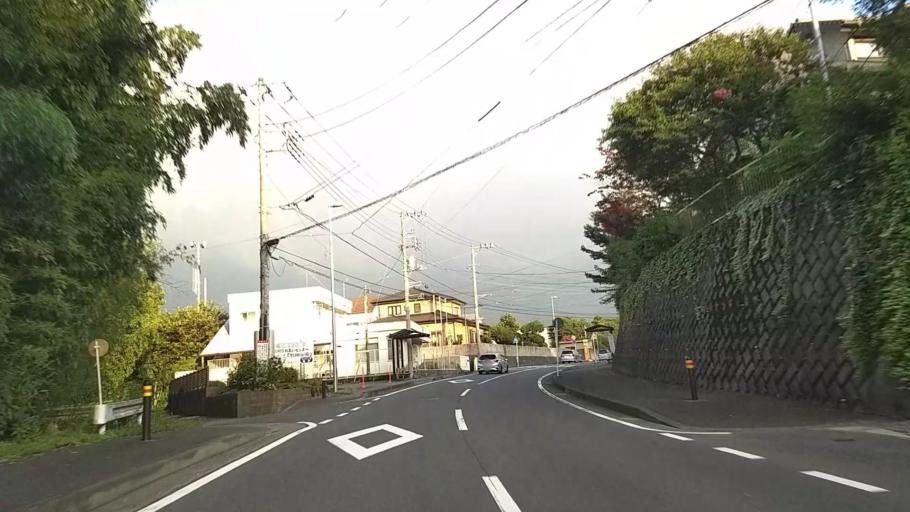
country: JP
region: Kanagawa
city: Atsugi
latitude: 35.4766
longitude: 139.2829
